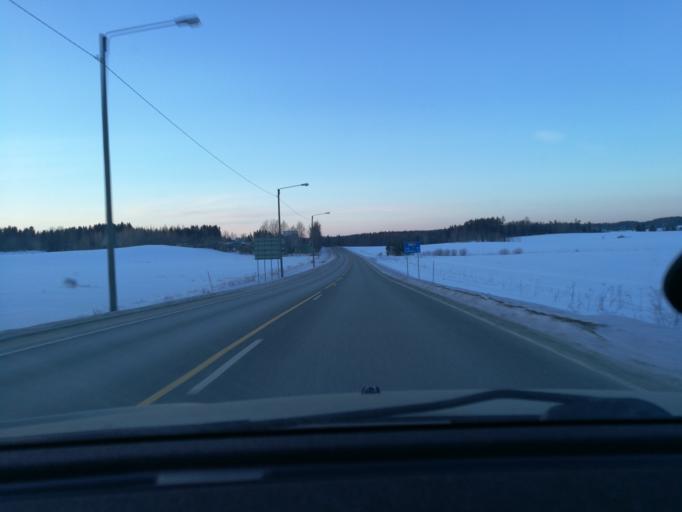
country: FI
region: Uusimaa
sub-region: Helsinki
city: Vihti
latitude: 60.4129
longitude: 24.4492
